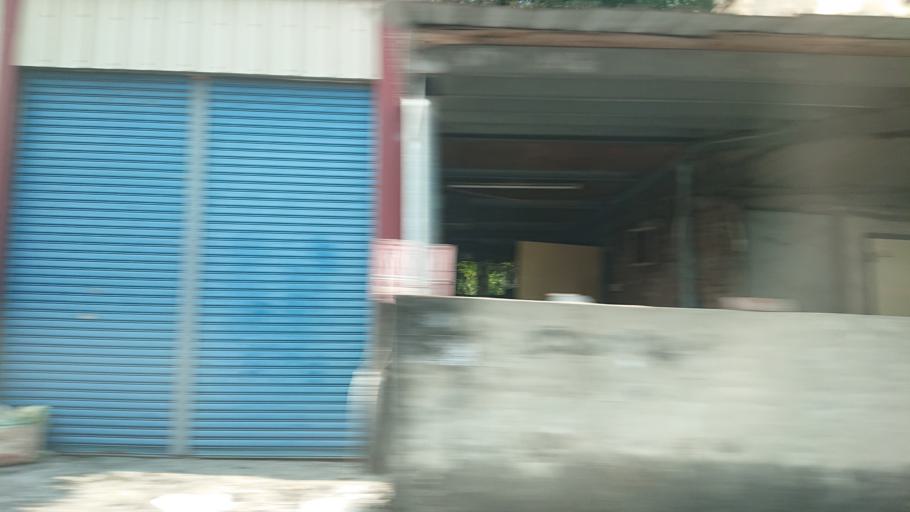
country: TW
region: Taiwan
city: Lugu
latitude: 23.7280
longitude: 120.6670
